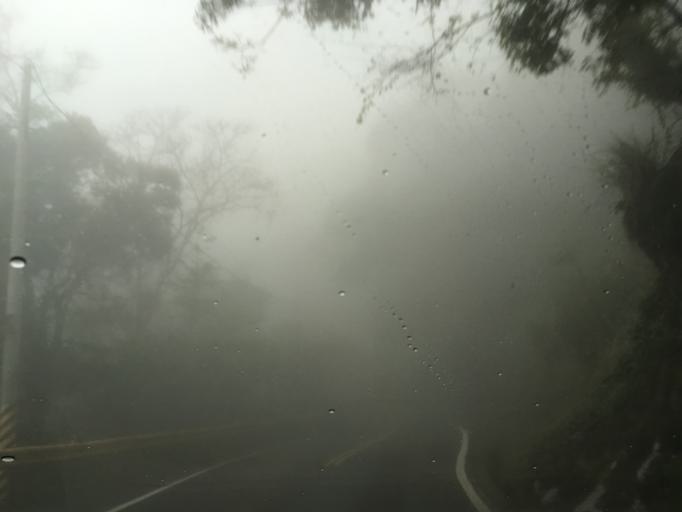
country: TW
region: Taiwan
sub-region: Hualien
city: Hualian
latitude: 24.1923
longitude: 121.4189
